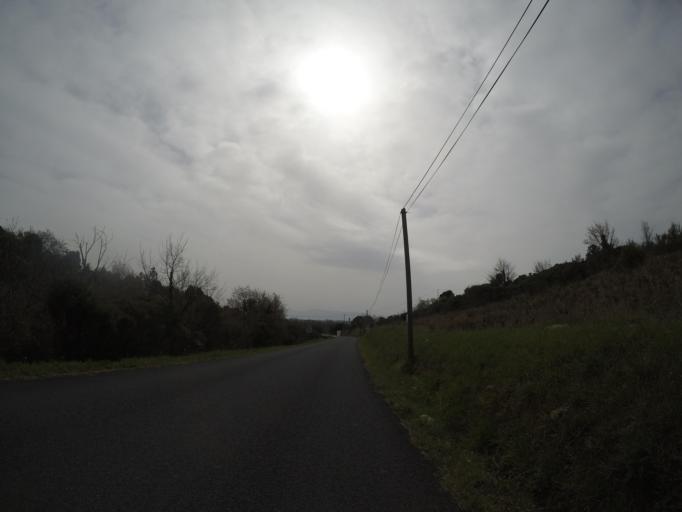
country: FR
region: Languedoc-Roussillon
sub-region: Departement des Pyrenees-Orientales
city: Pezilla-la-Riviere
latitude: 42.7052
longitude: 2.7625
